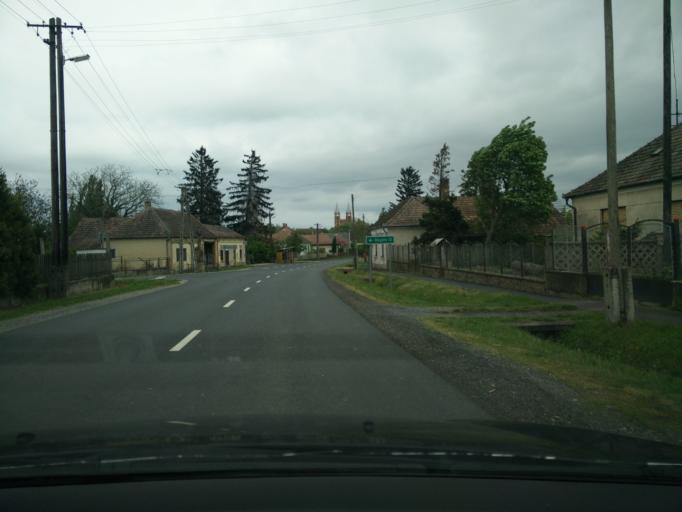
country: HU
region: Zala
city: Turje
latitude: 46.9863
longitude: 17.0984
